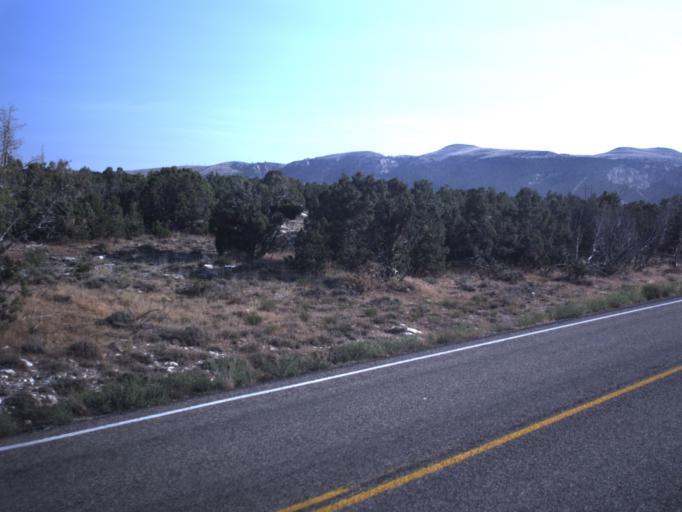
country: US
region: Utah
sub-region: Uintah County
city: Vernal
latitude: 40.6164
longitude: -109.4755
